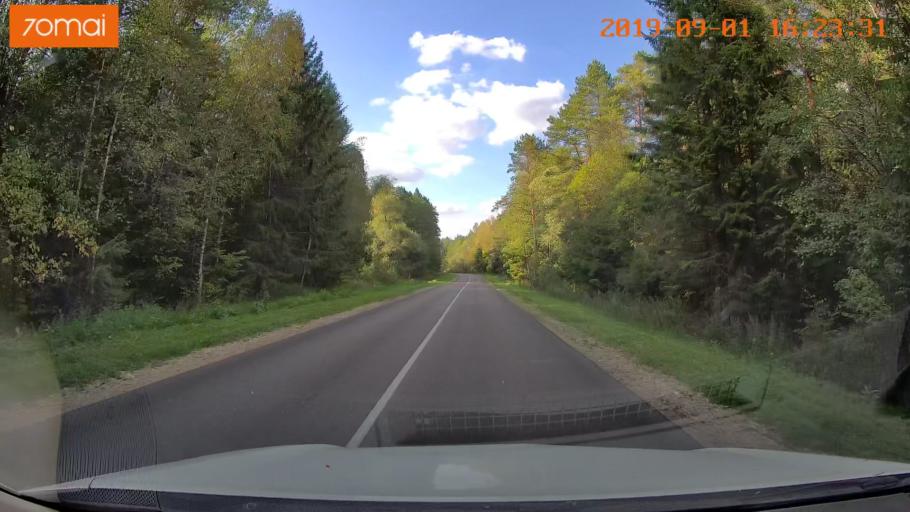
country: RU
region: Kaluga
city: Maloyaroslavets
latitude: 54.8819
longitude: 36.5322
